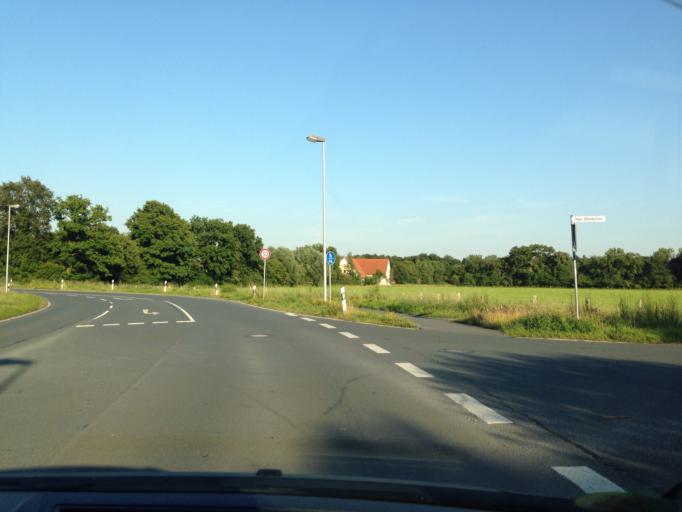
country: DE
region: North Rhine-Westphalia
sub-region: Regierungsbezirk Munster
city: Muenster
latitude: 51.9920
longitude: 7.5717
